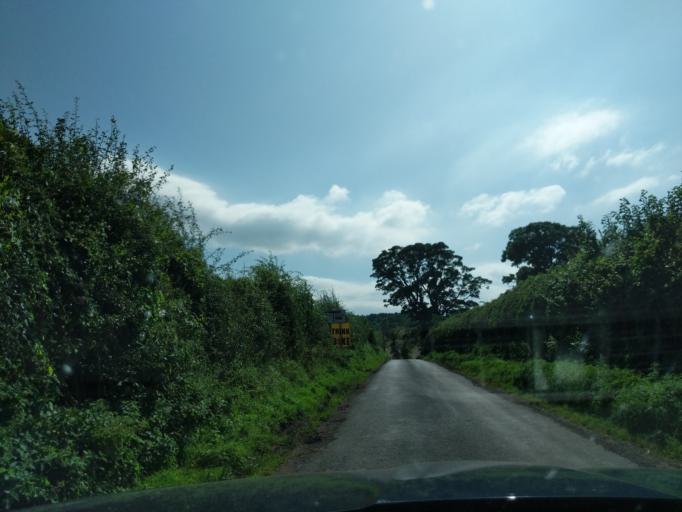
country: GB
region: England
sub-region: Northumberland
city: Ford
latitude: 55.6386
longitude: -2.1378
